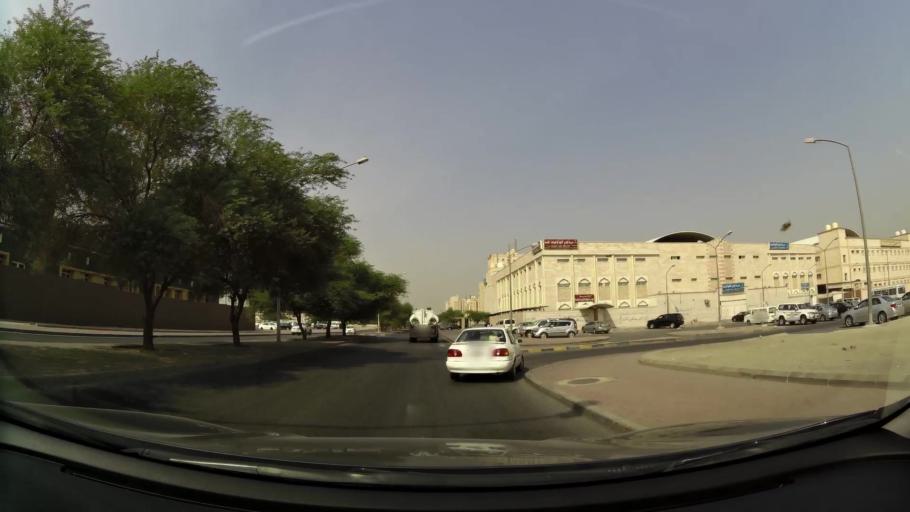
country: KW
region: Al Farwaniyah
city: Al Farwaniyah
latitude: 29.2508
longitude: 47.9289
